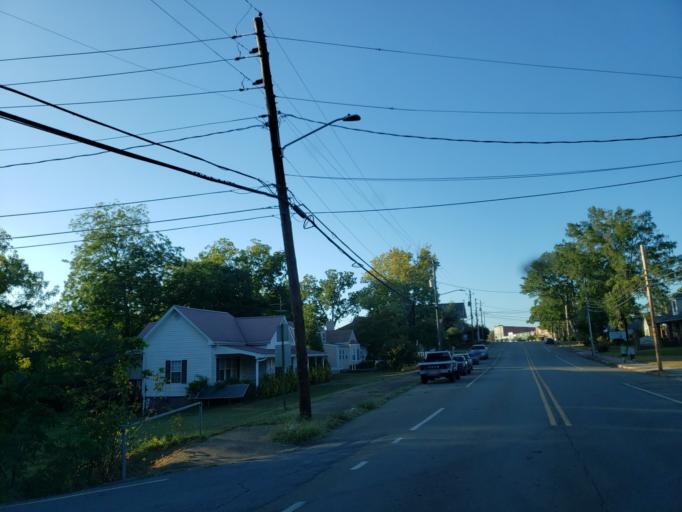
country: US
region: Georgia
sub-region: Pickens County
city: Jasper
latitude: 34.4655
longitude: -84.4289
